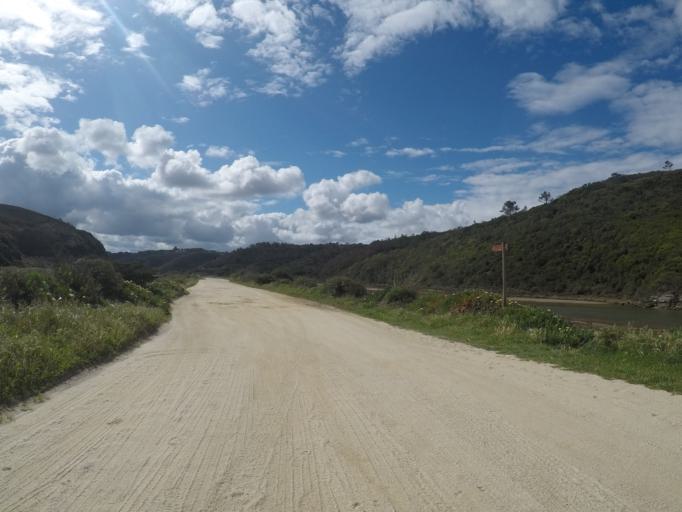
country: PT
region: Beja
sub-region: Odemira
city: Sao Teotonio
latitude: 37.4397
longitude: -8.7952
